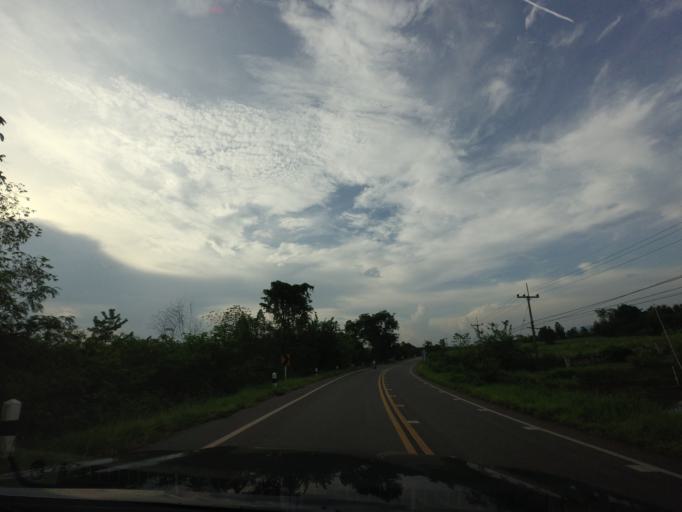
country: TH
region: Changwat Udon Thani
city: Nam Som
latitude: 17.8059
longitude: 102.2730
